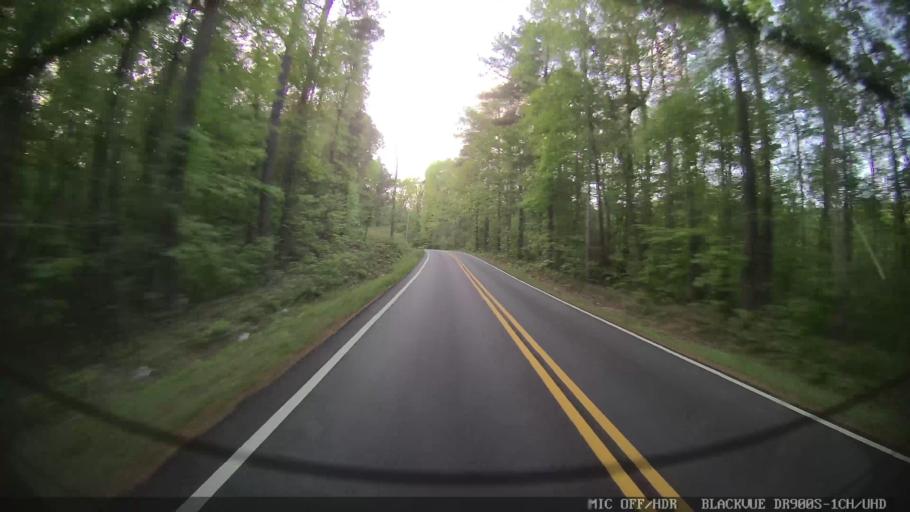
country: US
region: Georgia
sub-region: Bartow County
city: Emerson
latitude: 34.0876
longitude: -84.7653
